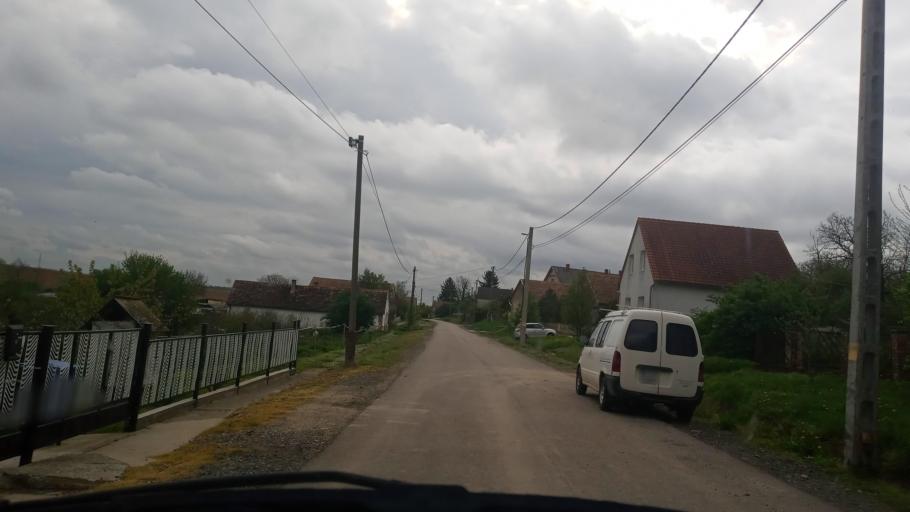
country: HU
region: Baranya
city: Boly
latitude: 45.9722
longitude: 18.4351
